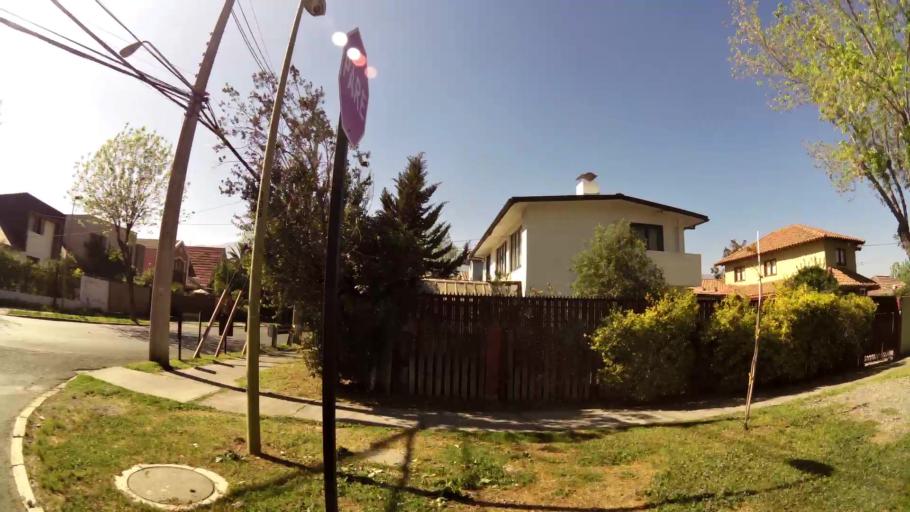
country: CL
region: Santiago Metropolitan
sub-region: Provincia de Santiago
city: Villa Presidente Frei, Nunoa, Santiago, Chile
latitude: -33.3991
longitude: -70.5506
